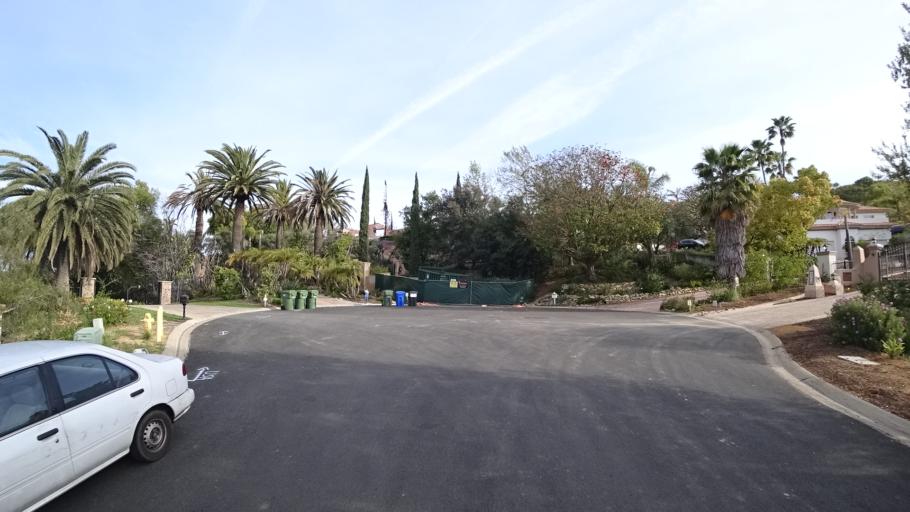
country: US
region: California
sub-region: Ventura County
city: Thousand Oaks
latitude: 34.1979
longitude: -118.8089
